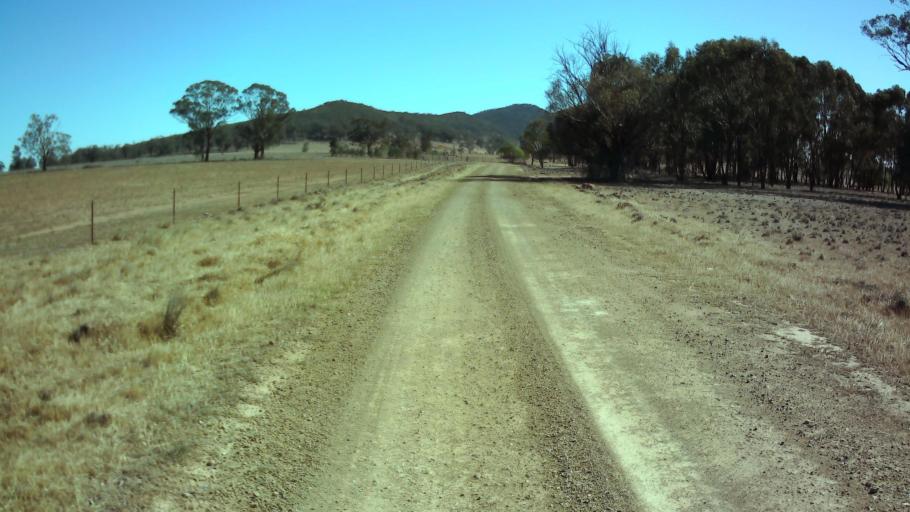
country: AU
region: New South Wales
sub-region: Weddin
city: Grenfell
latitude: -33.7652
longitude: 147.9236
